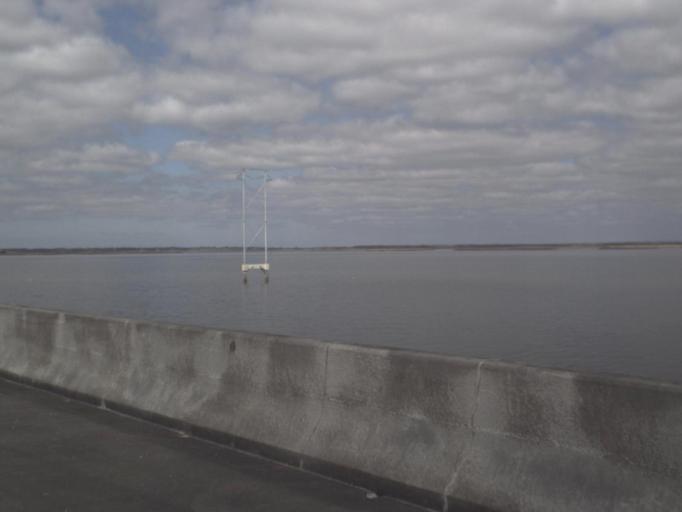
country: US
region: Florida
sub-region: Franklin County
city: Apalachicola
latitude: 29.7292
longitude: -84.9471
